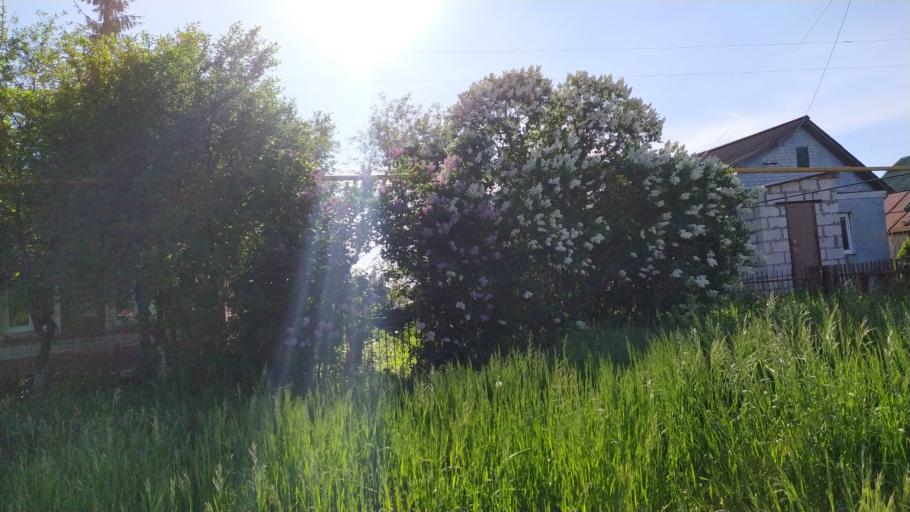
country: RU
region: Kursk
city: Kursk
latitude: 51.6385
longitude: 36.1487
